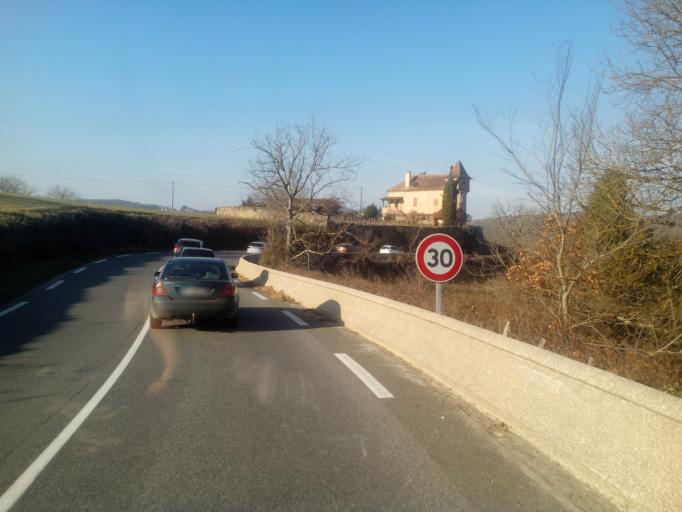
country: FR
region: Midi-Pyrenees
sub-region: Departement du Lot
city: Figeac
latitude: 44.6062
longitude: 2.0526
